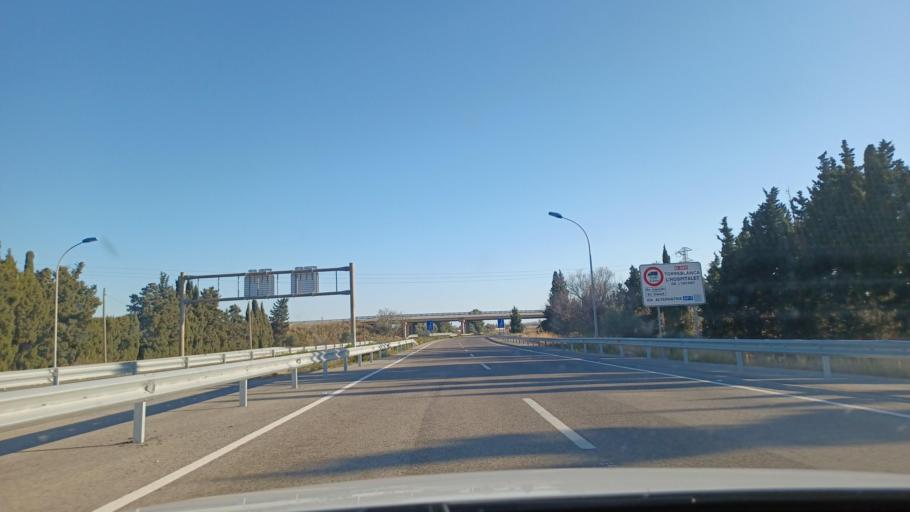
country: ES
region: Catalonia
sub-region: Provincia de Tarragona
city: Amposta
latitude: 40.7266
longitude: 0.5889
